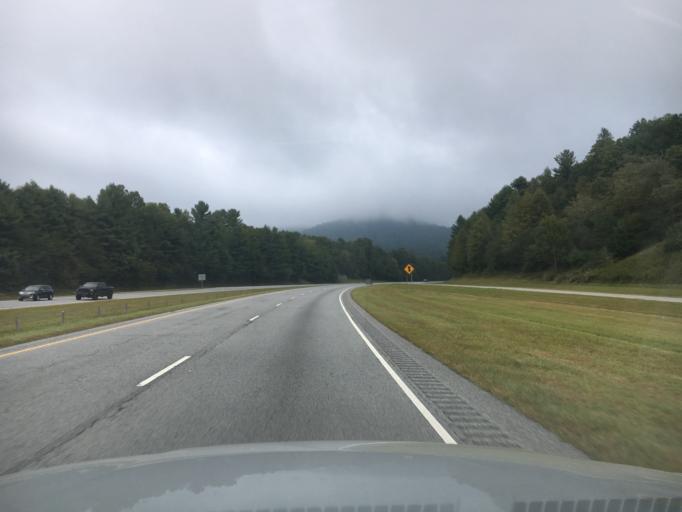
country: US
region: North Carolina
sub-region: Henderson County
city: Flat Rock
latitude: 35.2170
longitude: -82.4443
